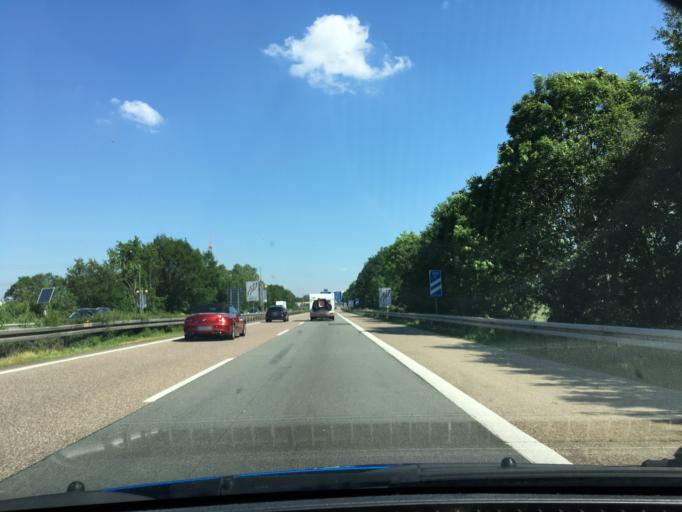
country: DE
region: North Rhine-Westphalia
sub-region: Regierungsbezirk Munster
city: Lotte
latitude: 52.2604
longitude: 7.9215
